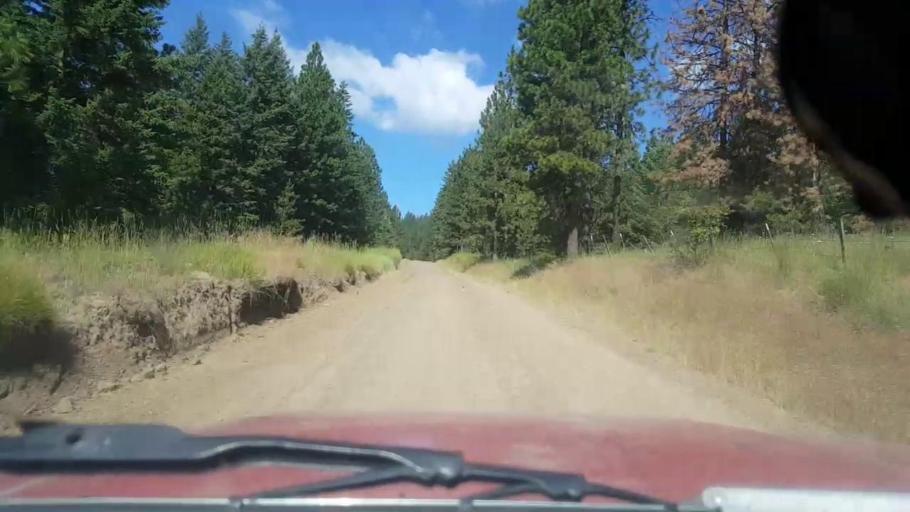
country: US
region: Washington
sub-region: Garfield County
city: Pomeroy
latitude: 46.0370
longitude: -117.4406
